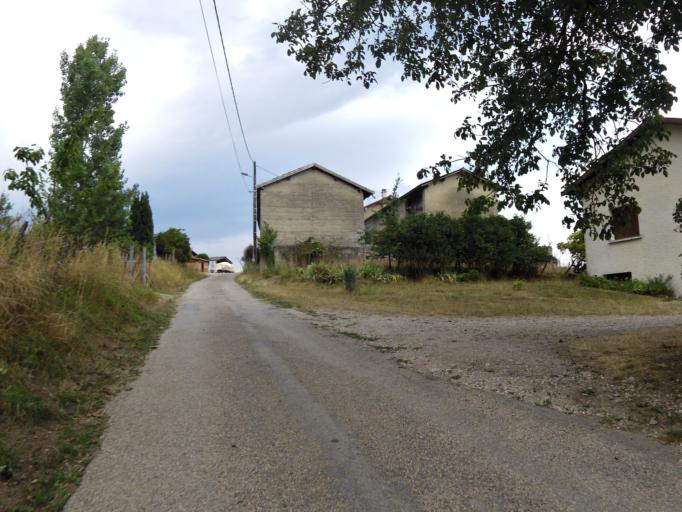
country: FR
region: Rhone-Alpes
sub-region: Departement de l'Ain
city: Perouges
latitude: 45.9111
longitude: 5.1780
